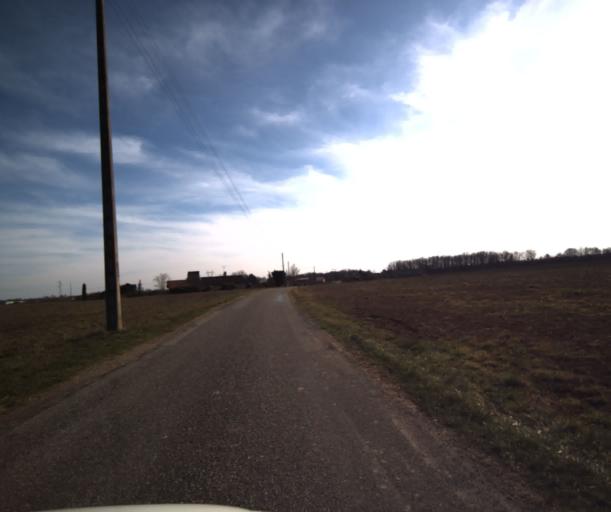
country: FR
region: Midi-Pyrenees
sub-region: Departement du Tarn-et-Garonne
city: Campsas
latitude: 43.9246
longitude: 1.3269
